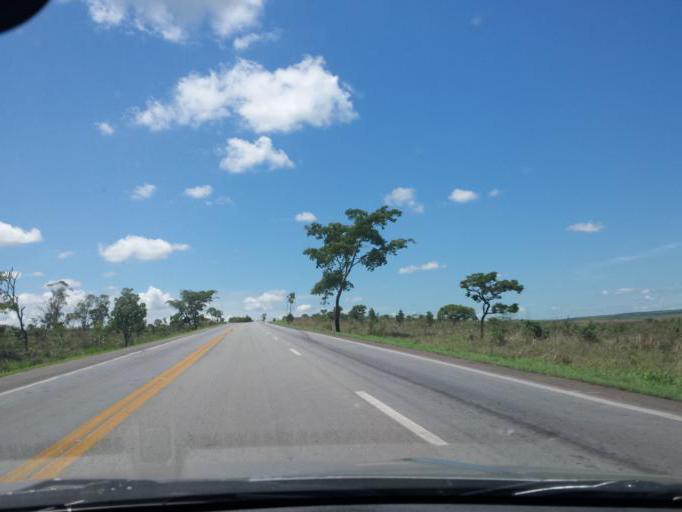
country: BR
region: Goias
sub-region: Cristalina
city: Cristalina
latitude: -16.5495
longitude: -47.7875
